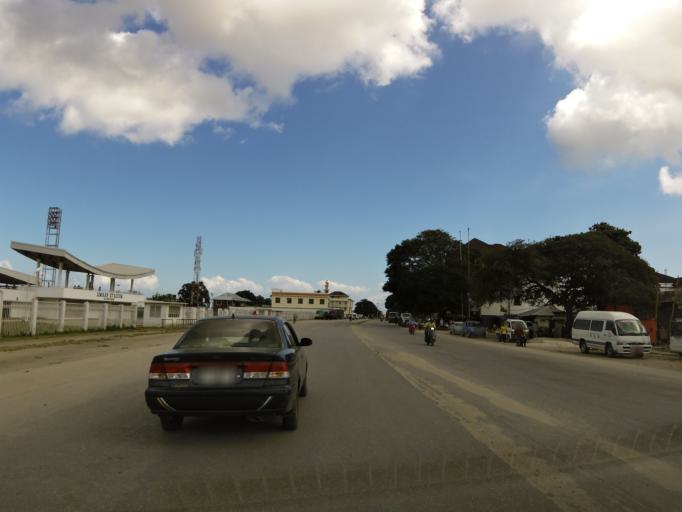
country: TZ
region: Zanzibar Urban/West
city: Zanzibar
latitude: -6.1648
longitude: 39.2247
